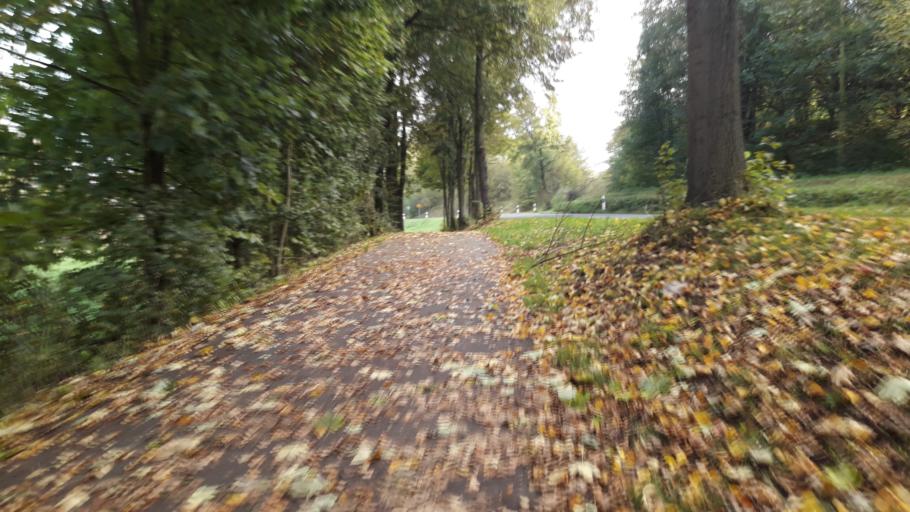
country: DE
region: North Rhine-Westphalia
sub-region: Regierungsbezirk Detmold
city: Paderborn
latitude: 51.6728
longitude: 8.7141
